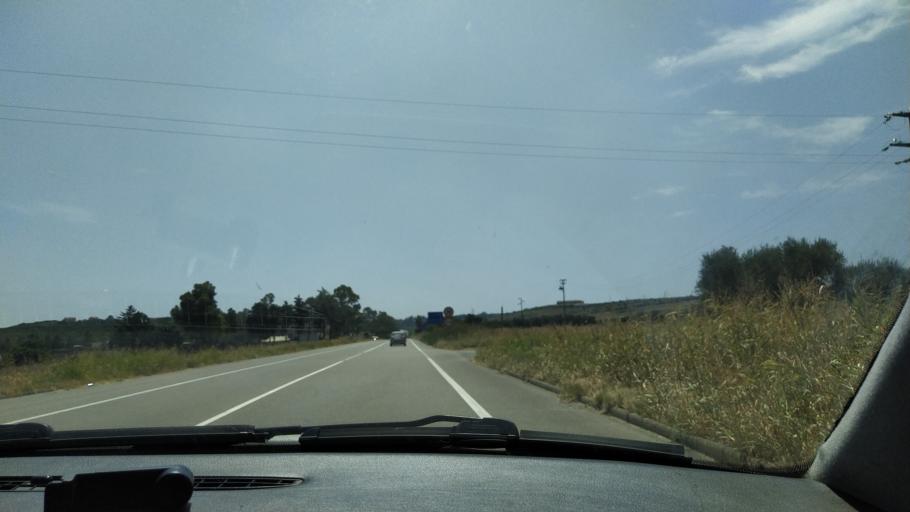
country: IT
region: Basilicate
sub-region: Provincia di Matera
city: Bernalda
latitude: 40.4464
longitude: 16.7782
